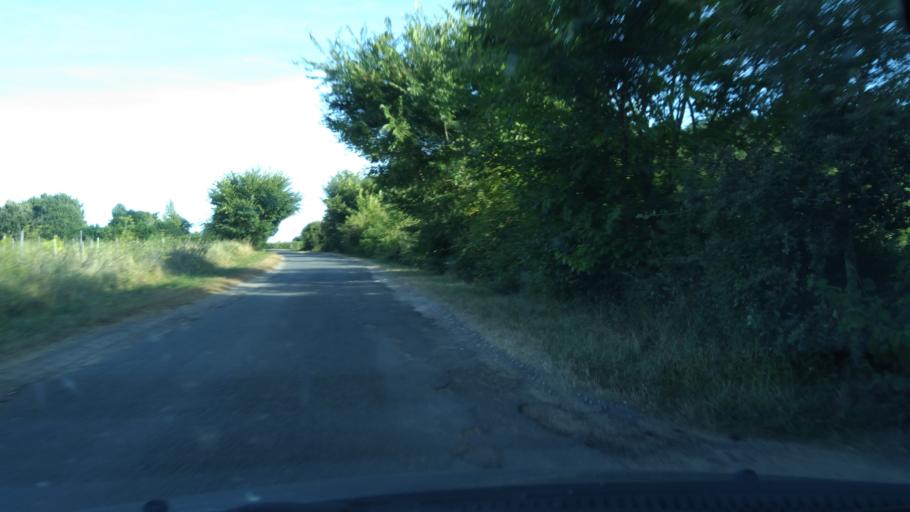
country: FR
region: Poitou-Charentes
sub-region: Departement de la Charente-Maritime
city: Dolus-d'Oleron
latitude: 45.9459
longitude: -1.3462
